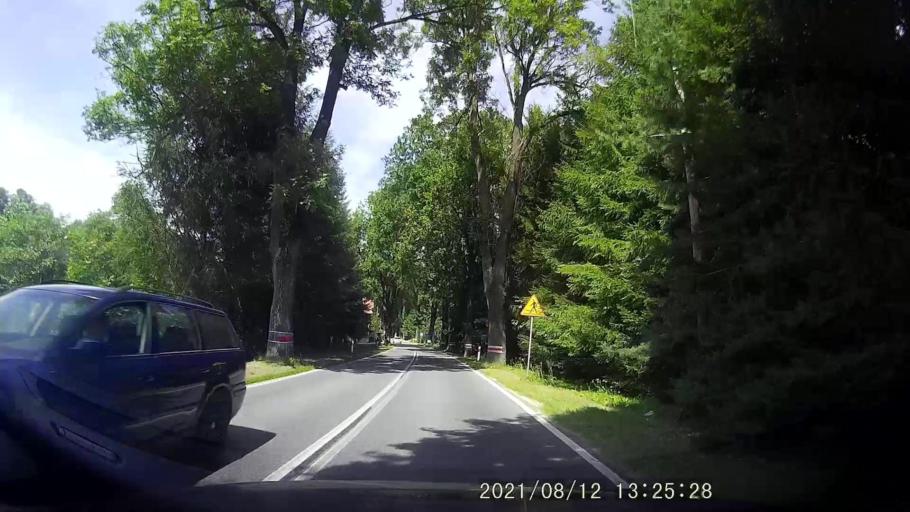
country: PL
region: Lower Silesian Voivodeship
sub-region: Powiat klodzki
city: Ladek-Zdroj
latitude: 50.3216
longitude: 16.8874
